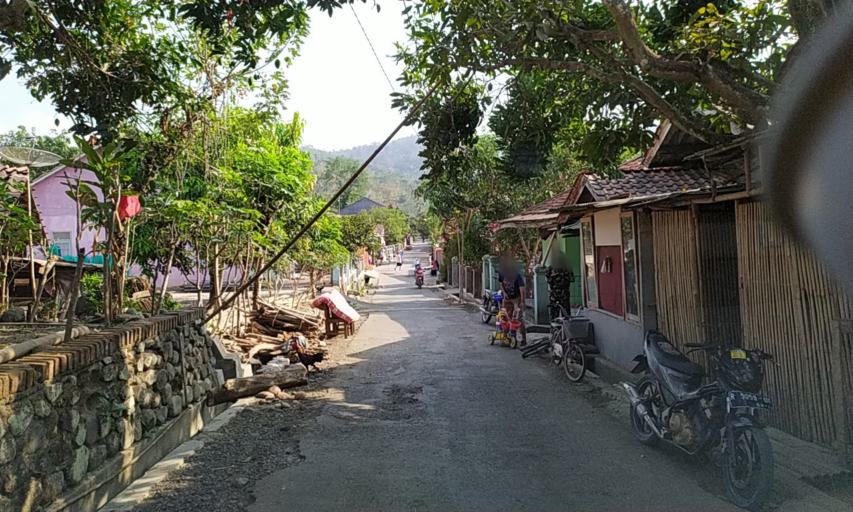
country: ID
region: Central Java
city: Jambuluwuk
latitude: -7.3210
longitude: 108.8785
